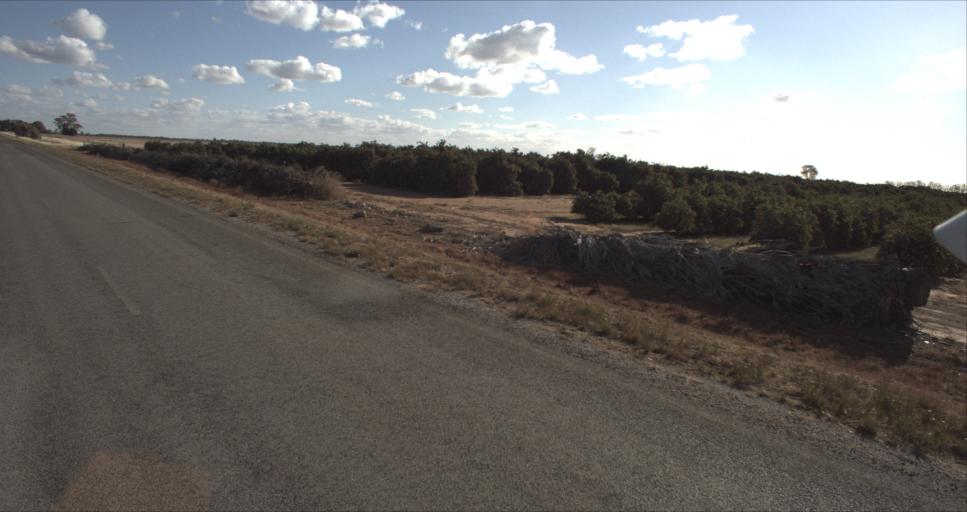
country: AU
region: New South Wales
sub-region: Leeton
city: Leeton
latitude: -34.5287
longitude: 146.2819
